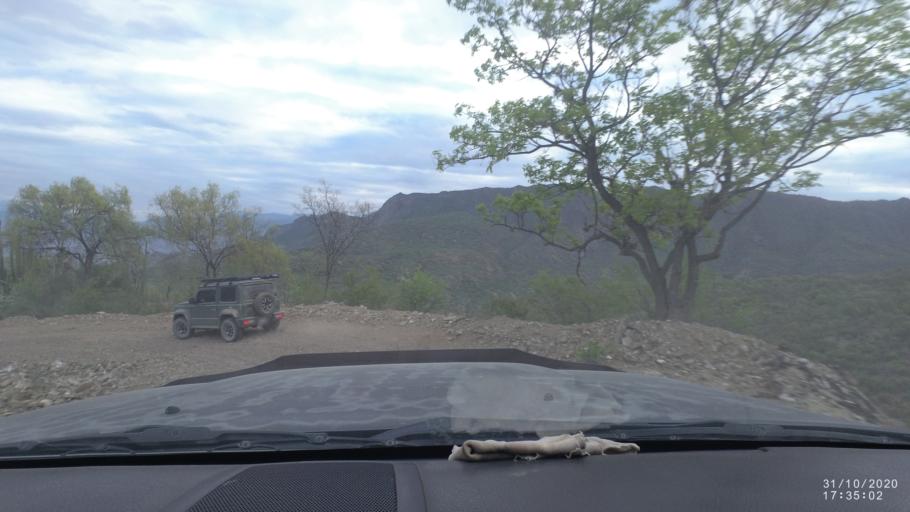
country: BO
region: Chuquisaca
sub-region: Provincia Zudanez
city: Mojocoya
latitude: -18.6026
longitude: -64.5482
